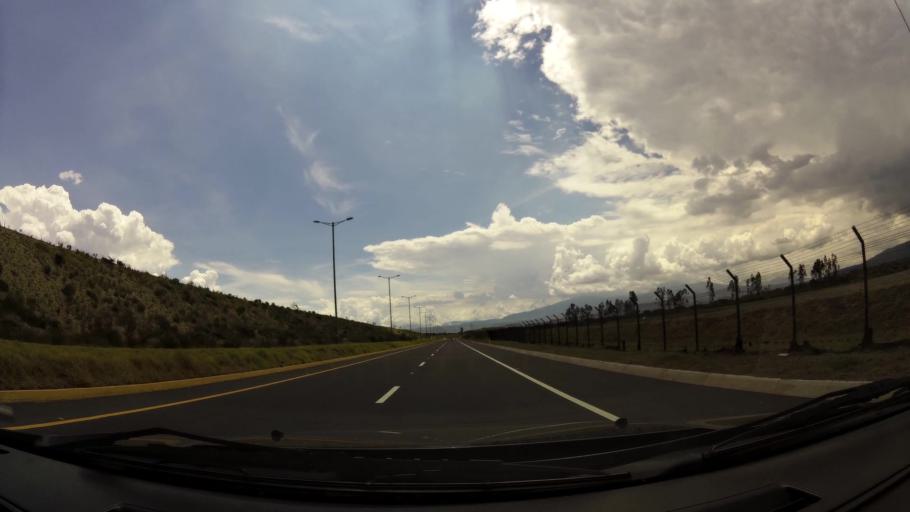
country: EC
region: Pichincha
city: Quito
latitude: -0.1089
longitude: -78.3657
